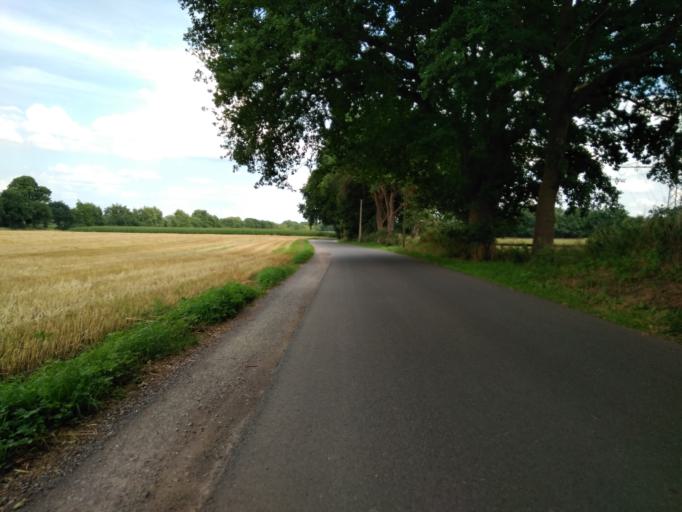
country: DE
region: North Rhine-Westphalia
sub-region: Regierungsbezirk Dusseldorf
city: Schermbeck
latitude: 51.6802
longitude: 6.8819
